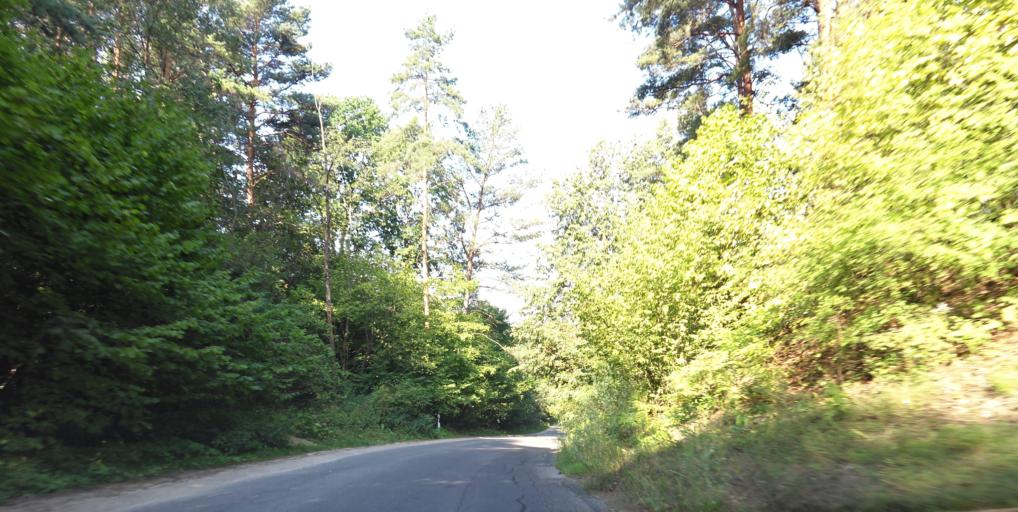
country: LT
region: Vilnius County
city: Pilaite
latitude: 54.6967
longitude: 25.1925
